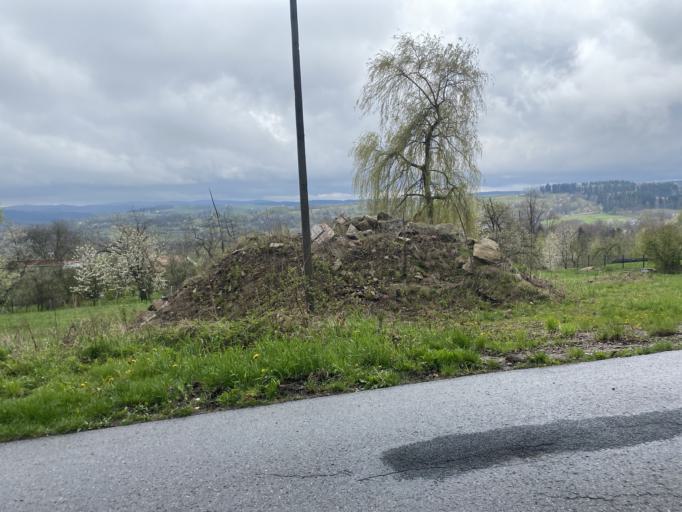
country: PL
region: Lesser Poland Voivodeship
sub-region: Powiat wadowicki
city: Kalwaria Zebrzydowska
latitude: 49.8546
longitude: 19.6673
